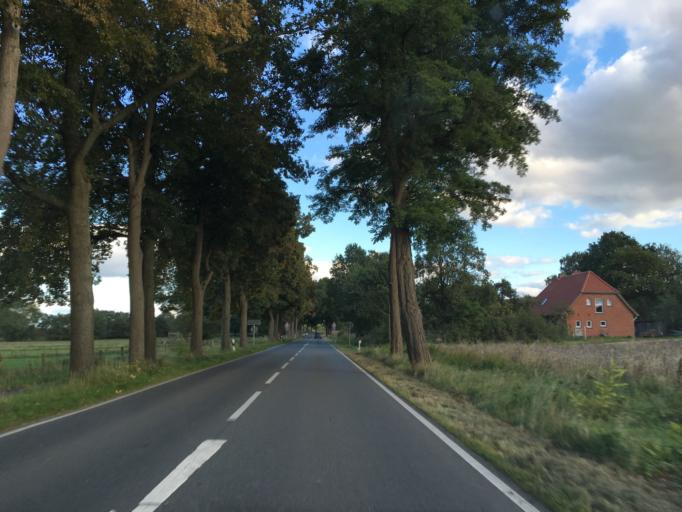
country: DE
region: Lower Saxony
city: Westergellersen
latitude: 53.2315
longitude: 10.2622
